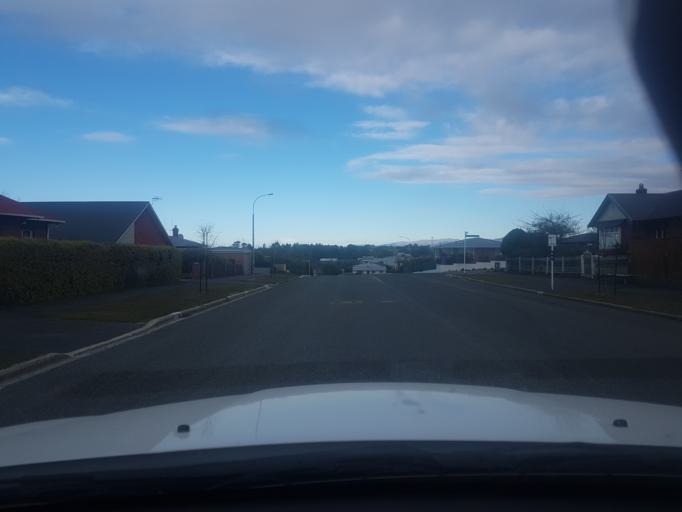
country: NZ
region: Canterbury
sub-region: Timaru District
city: Timaru
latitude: -44.3915
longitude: 171.2201
